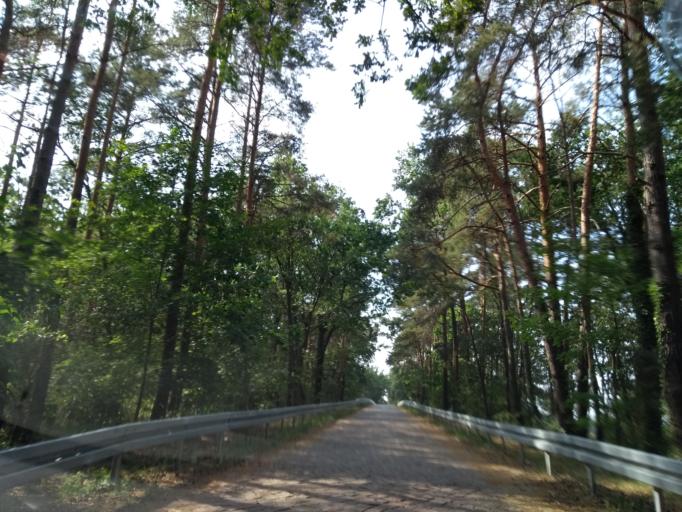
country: DE
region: Brandenburg
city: Lubbenau
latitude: 51.8384
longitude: 13.9213
